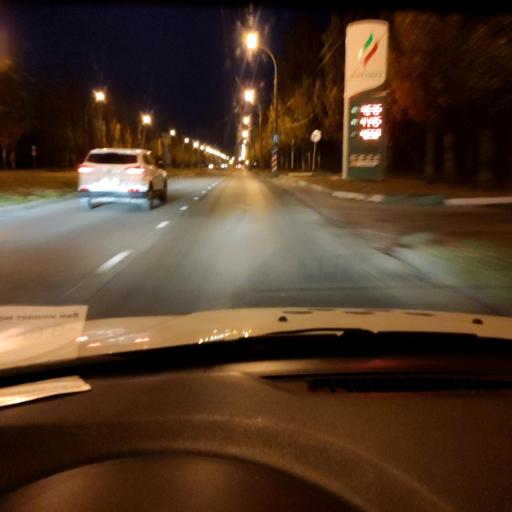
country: RU
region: Samara
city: Tol'yatti
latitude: 53.5502
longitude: 49.2704
